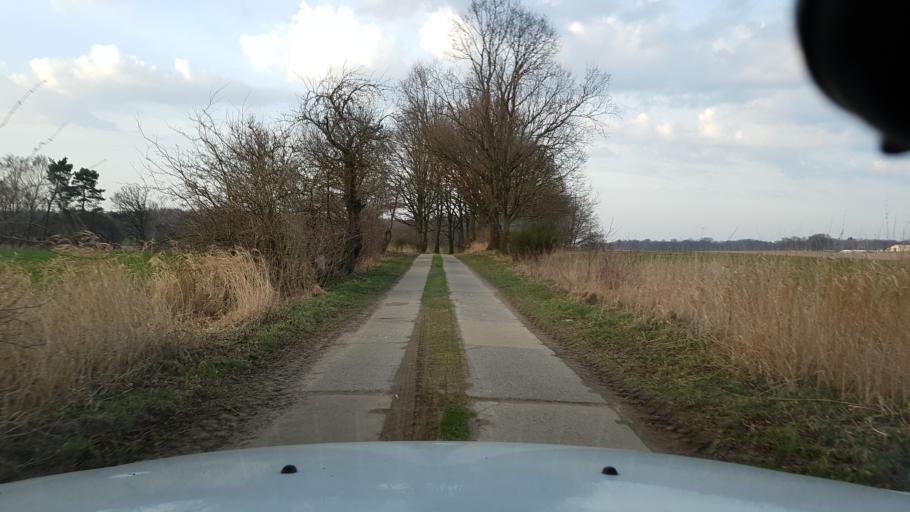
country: PL
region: West Pomeranian Voivodeship
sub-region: Koszalin
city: Koszalin
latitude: 54.0960
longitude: 16.1397
